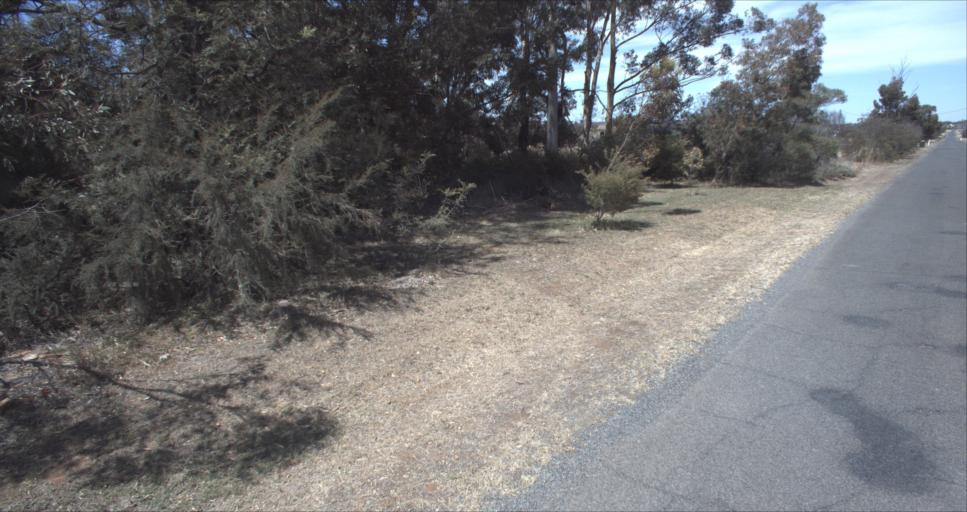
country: AU
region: New South Wales
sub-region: Leeton
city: Leeton
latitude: -34.5951
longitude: 146.4281
